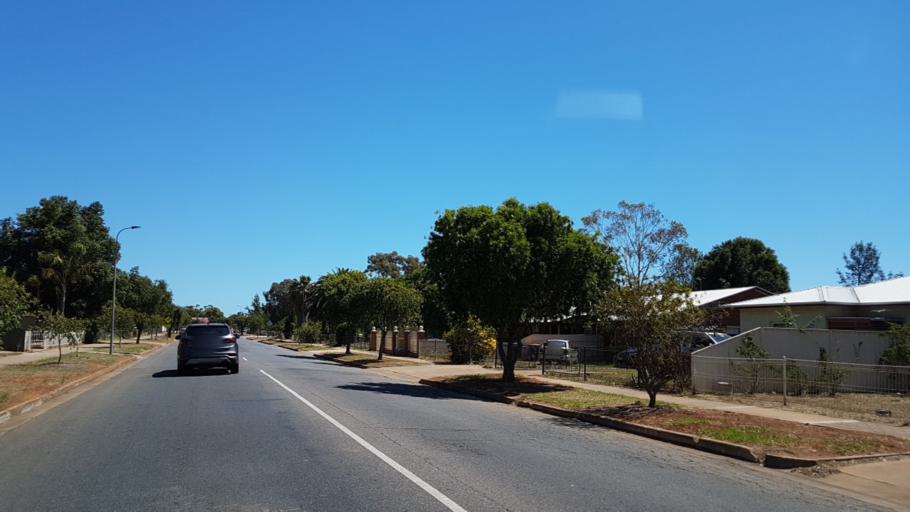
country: AU
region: South Australia
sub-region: Salisbury
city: Elizabeth
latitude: -34.7290
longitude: 138.6609
